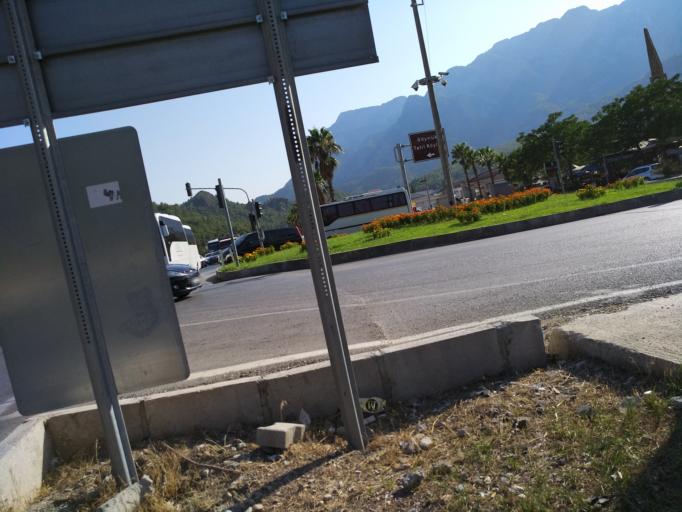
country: TR
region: Antalya
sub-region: Kemer
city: Goeynuek
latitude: 36.6669
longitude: 30.5519
